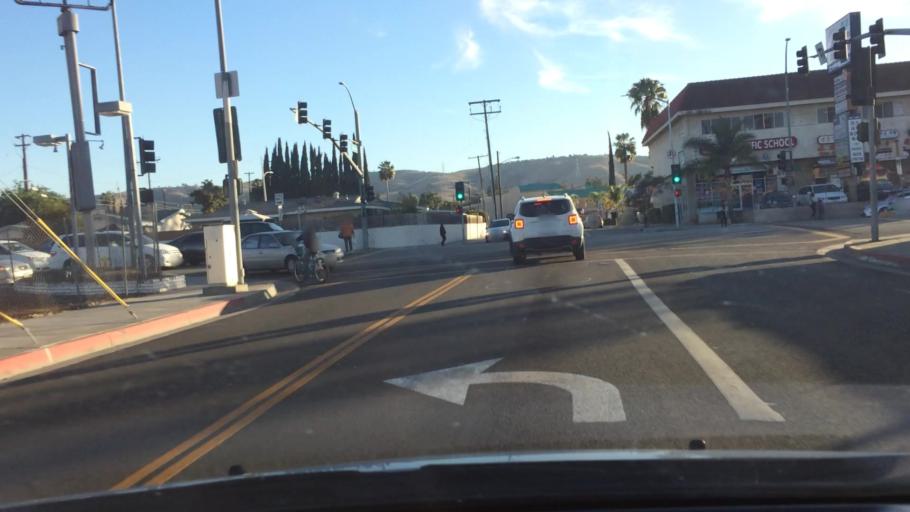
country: US
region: California
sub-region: Los Angeles County
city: Rowland Heights
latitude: 33.9886
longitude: -117.9012
